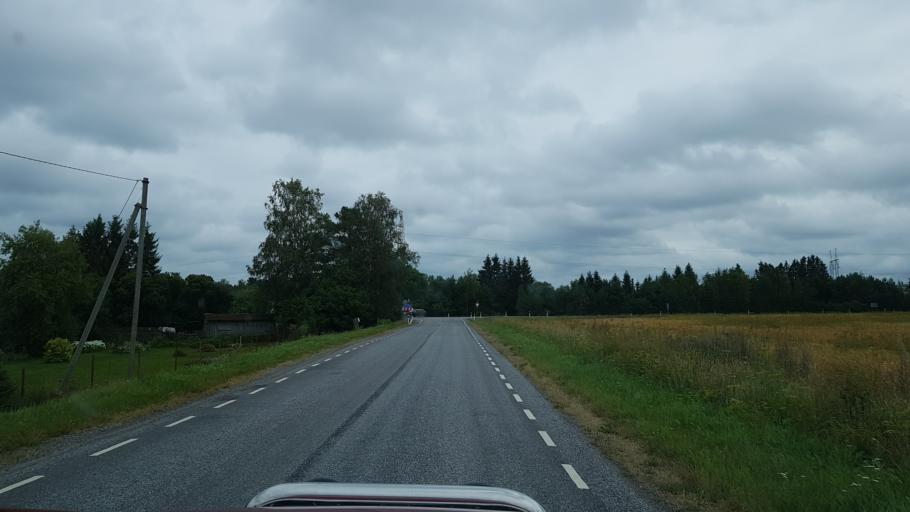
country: EE
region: Ida-Virumaa
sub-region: Puessi linn
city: Pussi
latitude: 59.3731
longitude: 27.0387
